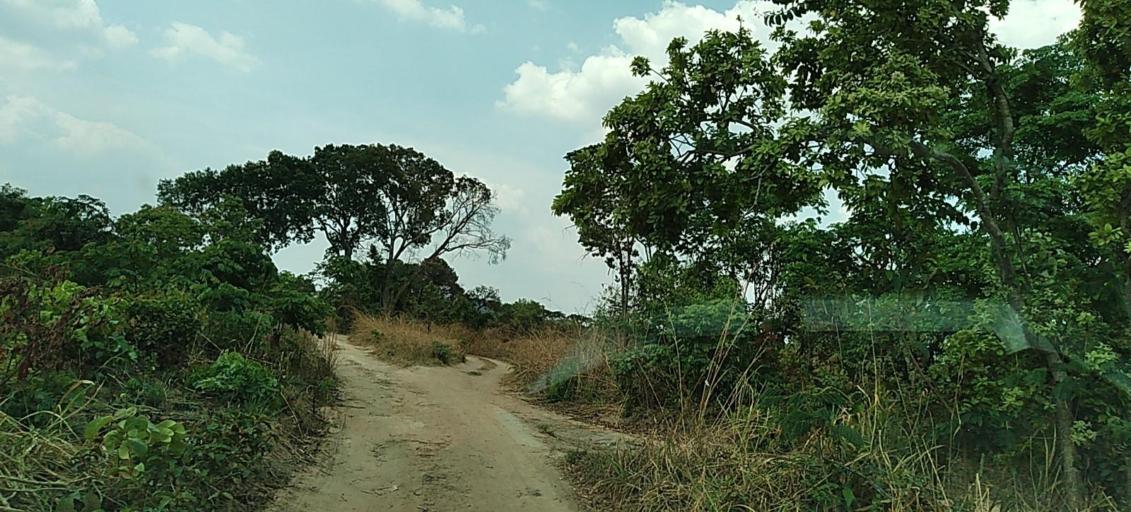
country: ZM
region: Copperbelt
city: Chililabombwe
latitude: -12.3210
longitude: 27.7489
